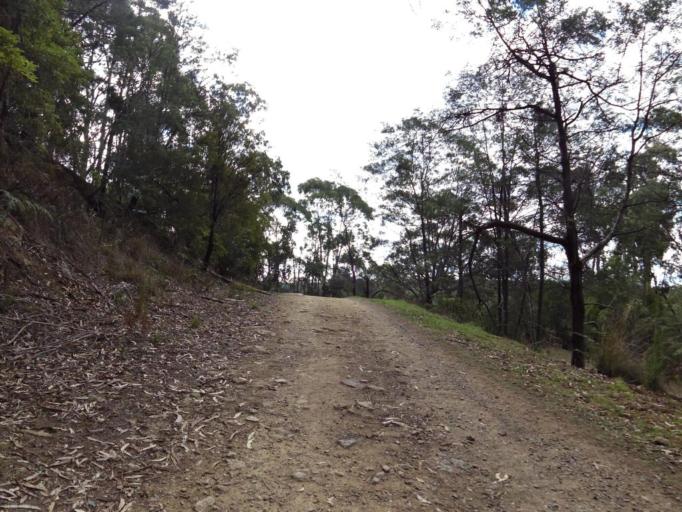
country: AU
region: Victoria
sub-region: Yarra Ranges
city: Mount Evelyn
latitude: -37.7990
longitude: 145.3839
